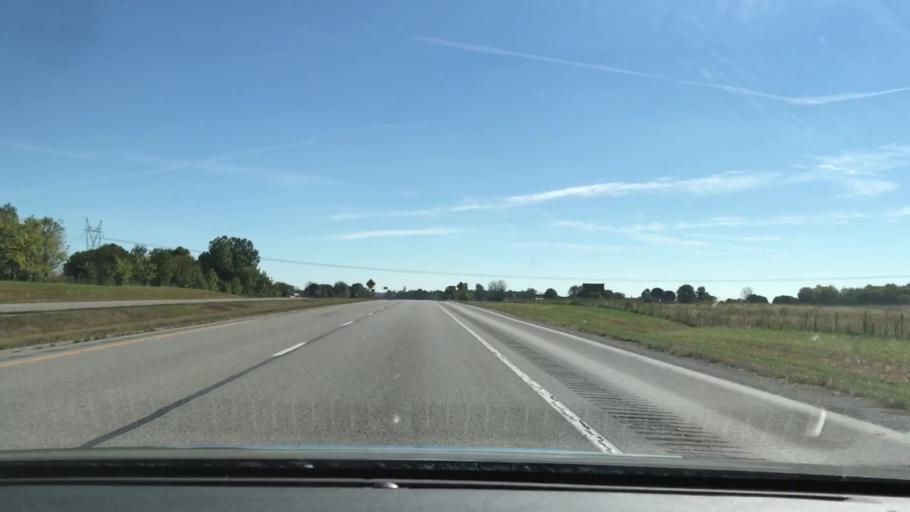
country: US
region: Kentucky
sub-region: Todd County
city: Elkton
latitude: 36.8232
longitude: -87.2024
